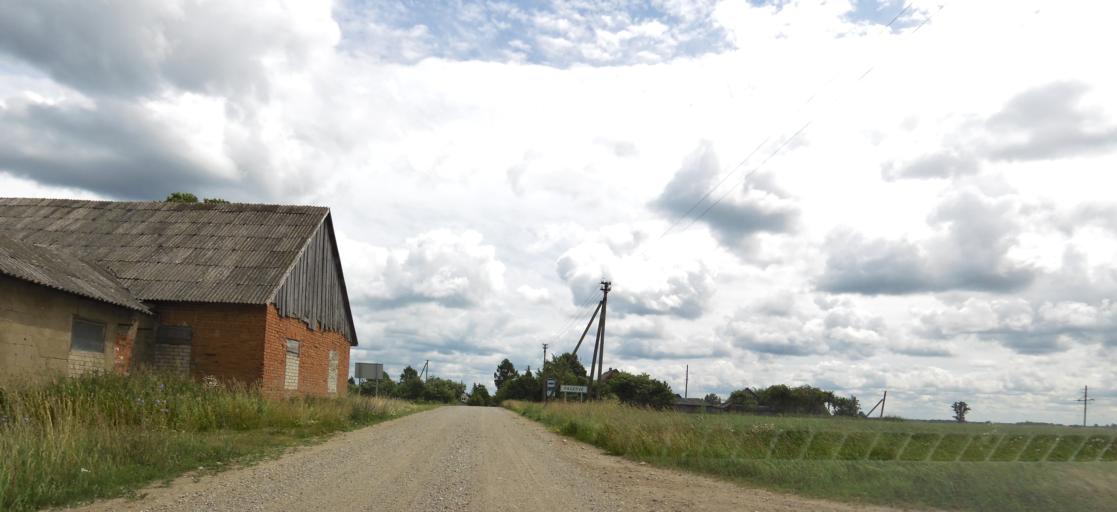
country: LT
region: Panevezys
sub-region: Birzai
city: Birzai
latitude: 56.3170
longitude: 24.7935
